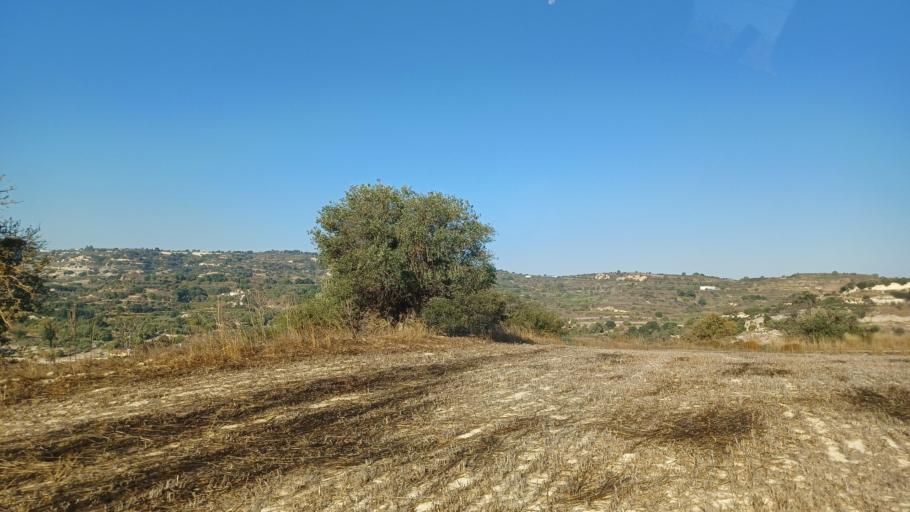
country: CY
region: Pafos
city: Mesogi
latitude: 34.8602
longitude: 32.5144
